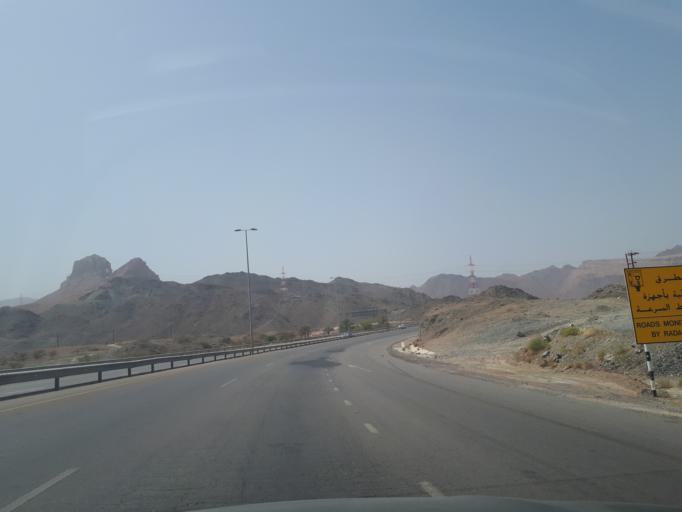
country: OM
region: Muhafazat ad Dakhiliyah
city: Bidbid
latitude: 23.4831
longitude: 58.1989
